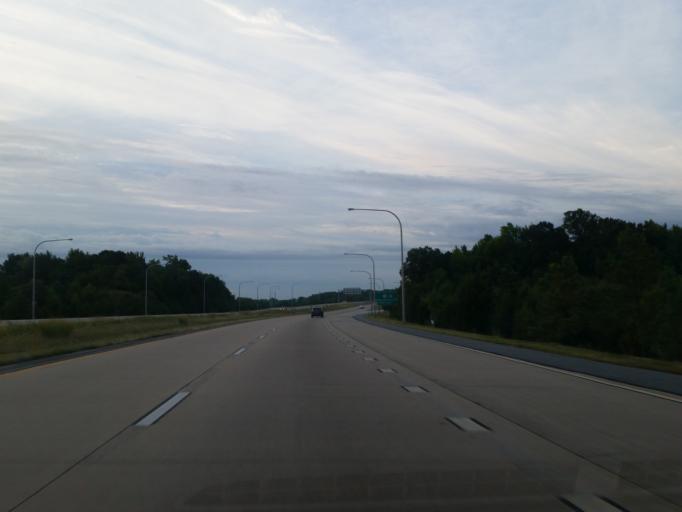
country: US
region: Delaware
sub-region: Kent County
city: Dover
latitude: 39.1723
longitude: -75.4969
